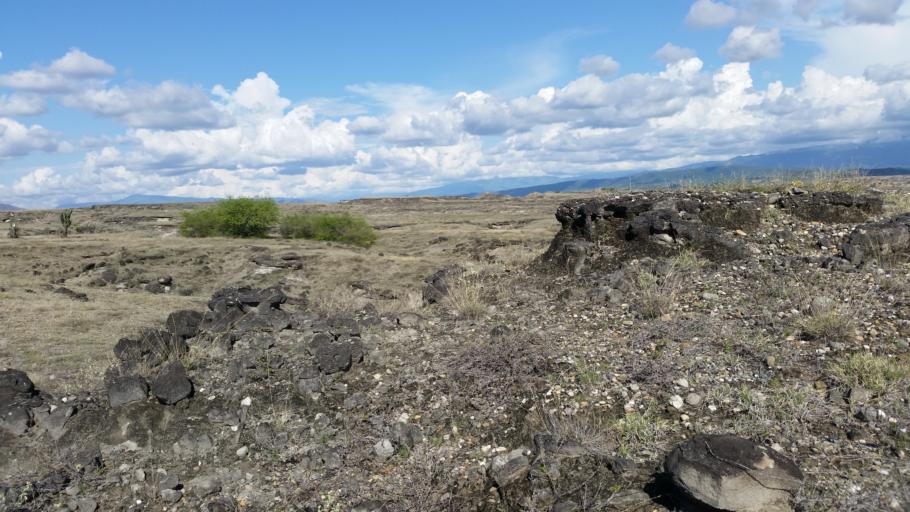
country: CO
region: Huila
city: Villavieja
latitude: 3.2528
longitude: -75.1449
